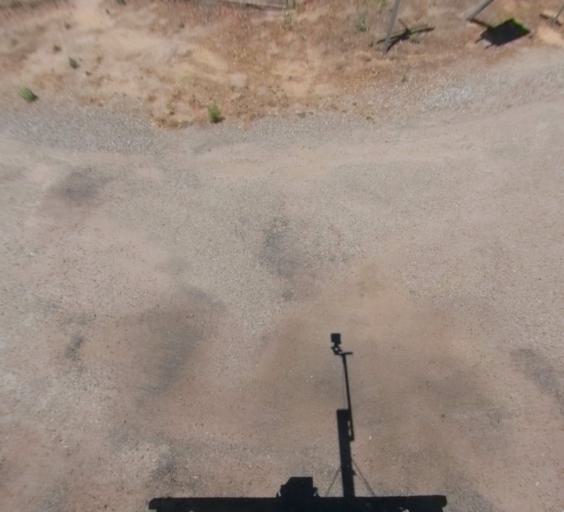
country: US
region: California
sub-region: Madera County
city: Bonadelle Ranchos-Madera Ranchos
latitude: 36.8658
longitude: -119.8390
